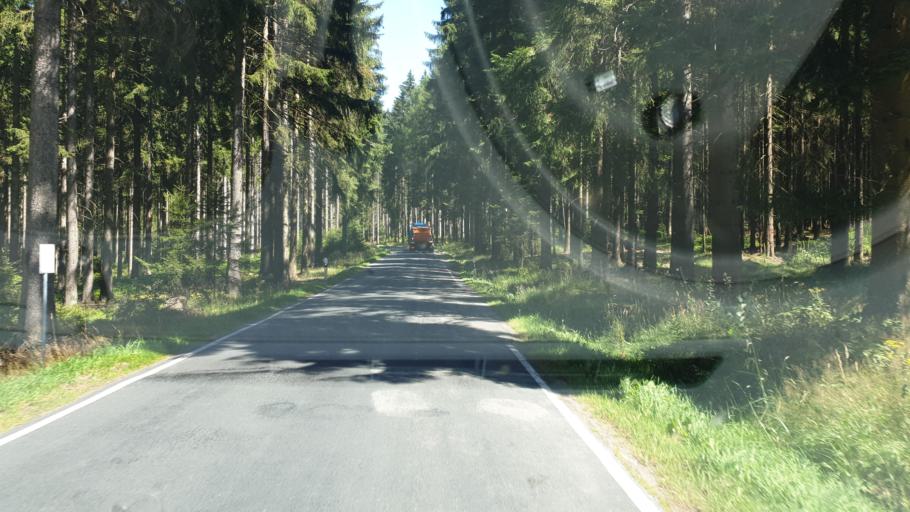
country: DE
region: Saxony
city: Bockau
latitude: 50.5062
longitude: 12.7049
